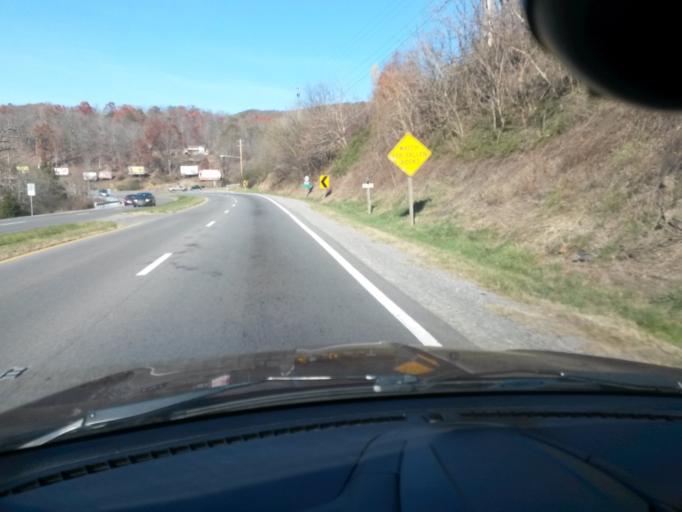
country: US
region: Virginia
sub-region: Roanoke County
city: Narrows
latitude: 37.1896
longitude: -79.9362
